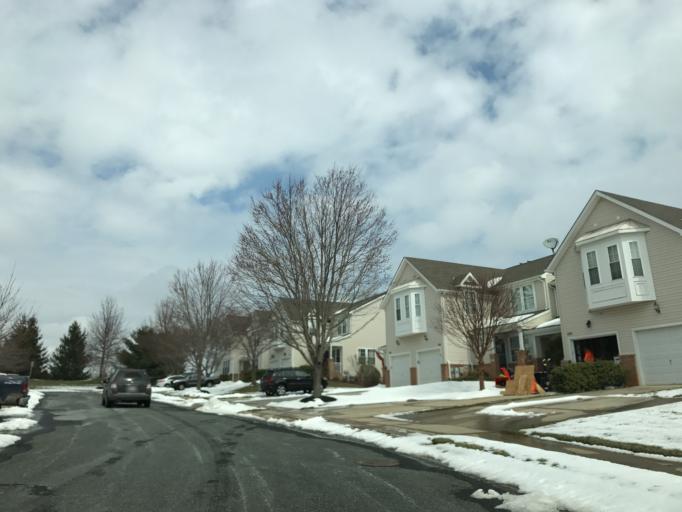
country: US
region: Maryland
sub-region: Harford County
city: Bel Air North
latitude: 39.5747
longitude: -76.3798
